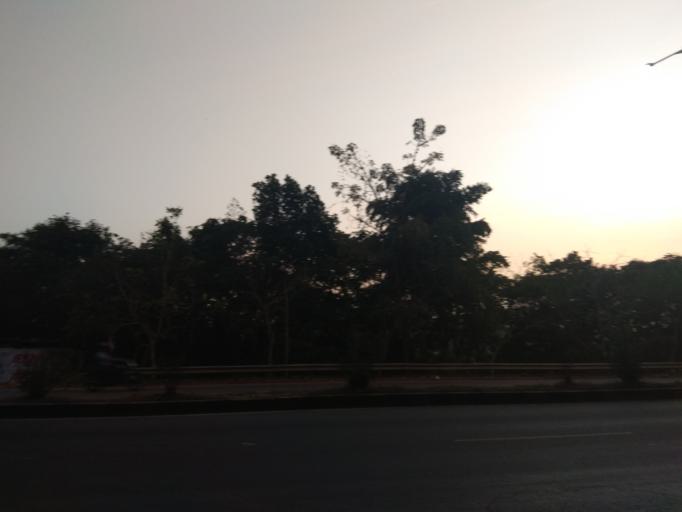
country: IN
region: Karnataka
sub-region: Dakshina Kannada
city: Mangalore
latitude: 12.8917
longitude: 74.8520
